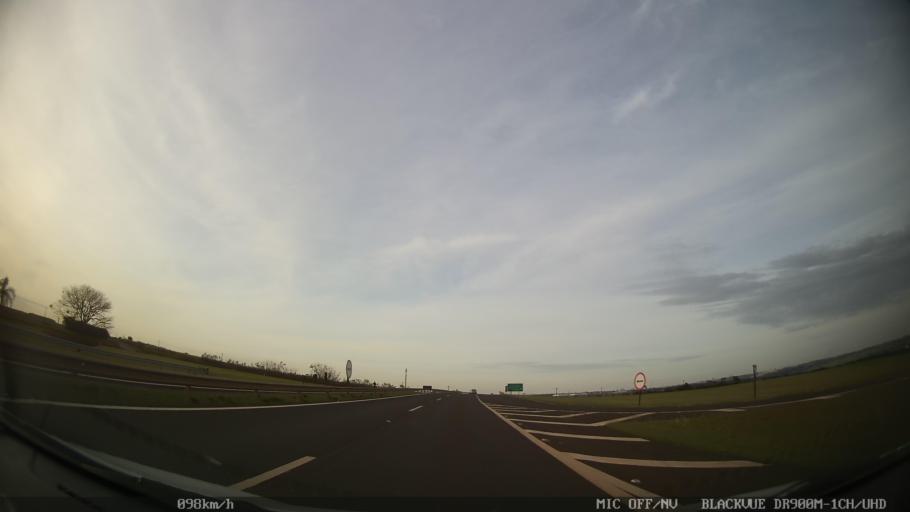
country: BR
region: Sao Paulo
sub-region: Iracemapolis
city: Iracemapolis
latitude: -22.6324
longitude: -47.5056
